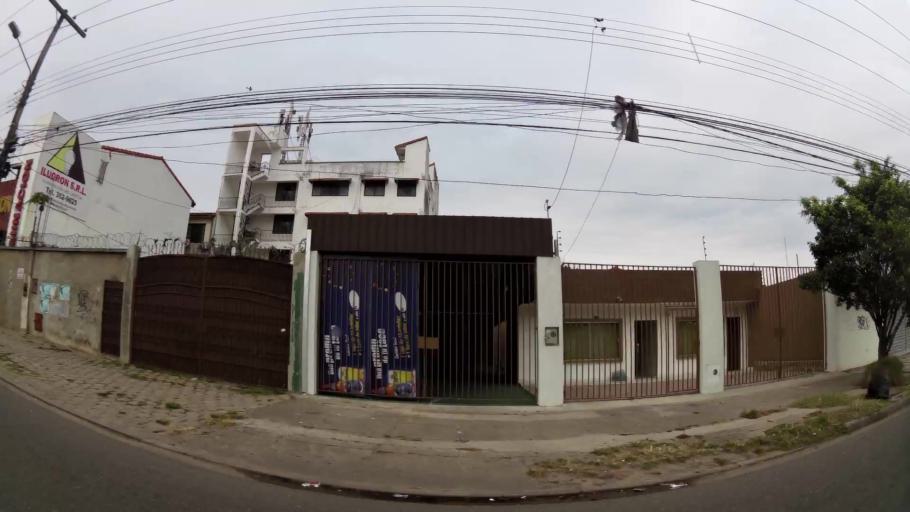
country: BO
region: Santa Cruz
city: Santa Cruz de la Sierra
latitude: -17.7879
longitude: -63.1946
